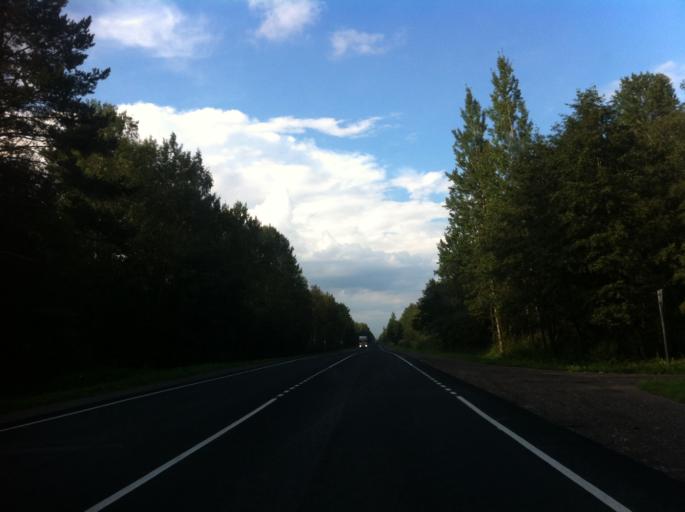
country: RU
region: Leningrad
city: Luga
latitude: 58.4669
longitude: 29.7674
